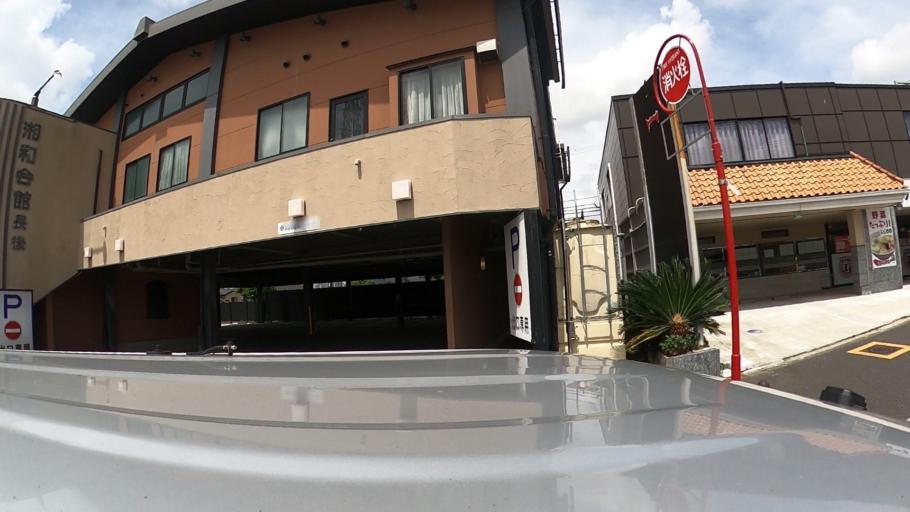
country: JP
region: Kanagawa
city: Fujisawa
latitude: 35.4136
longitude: 139.4700
